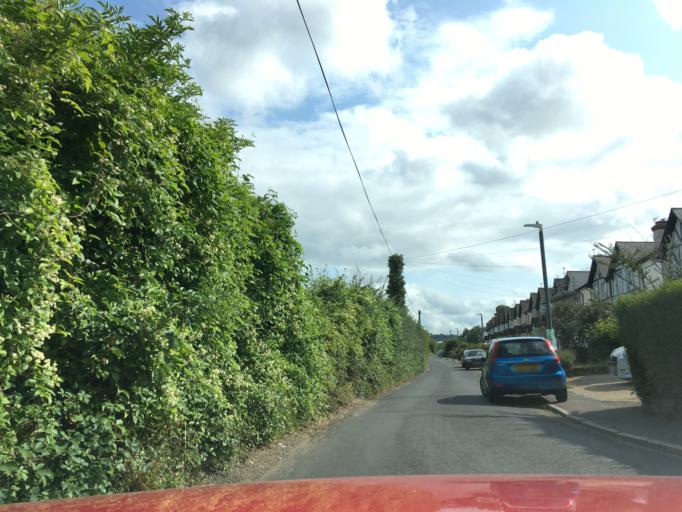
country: GB
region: England
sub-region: Kent
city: Maidstone
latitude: 51.2492
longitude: 0.5122
